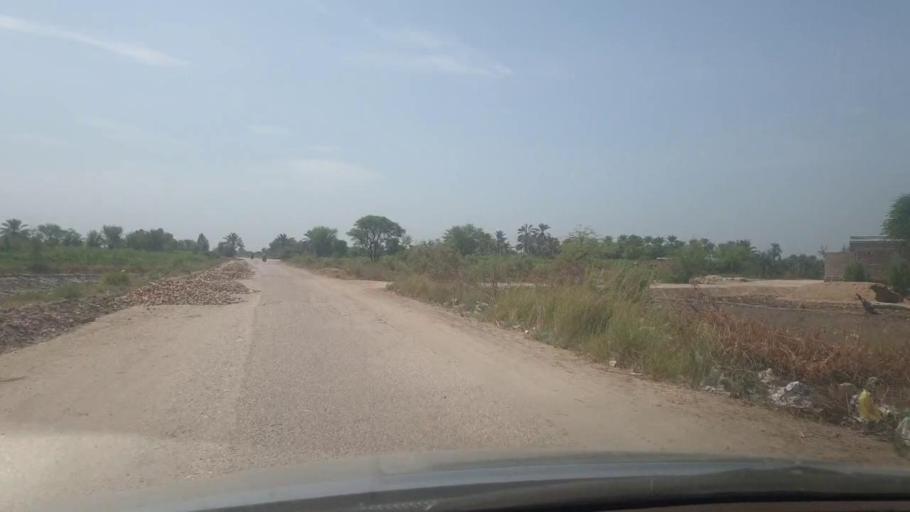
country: PK
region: Sindh
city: Bozdar
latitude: 27.2217
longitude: 68.5666
